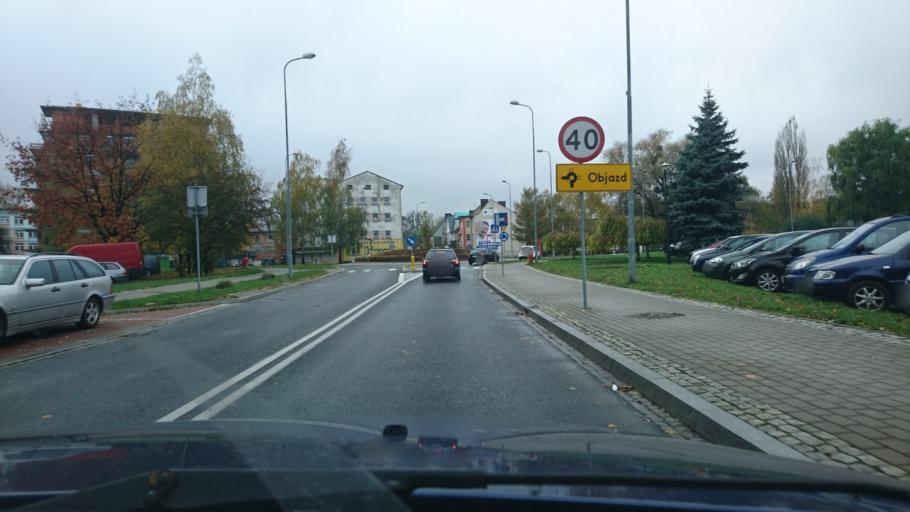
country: PL
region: Silesian Voivodeship
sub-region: Bielsko-Biala
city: Bielsko-Biala
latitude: 49.8199
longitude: 19.0513
